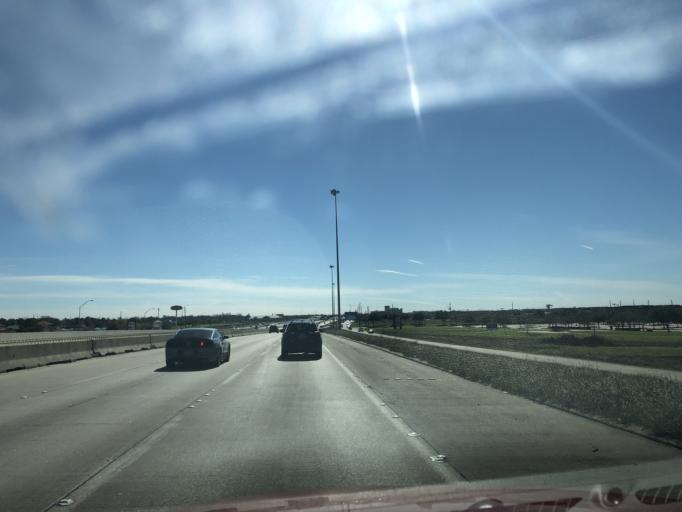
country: US
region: Texas
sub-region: Brazoria County
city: Brookside Village
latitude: 29.5794
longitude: -95.3865
